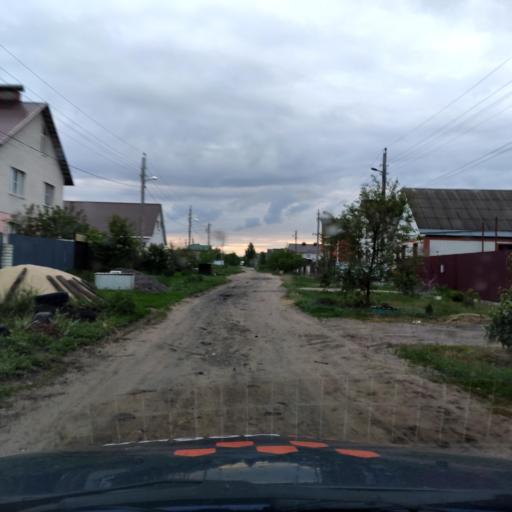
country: RU
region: Voronezj
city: Maslovka
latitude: 51.5430
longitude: 39.2392
